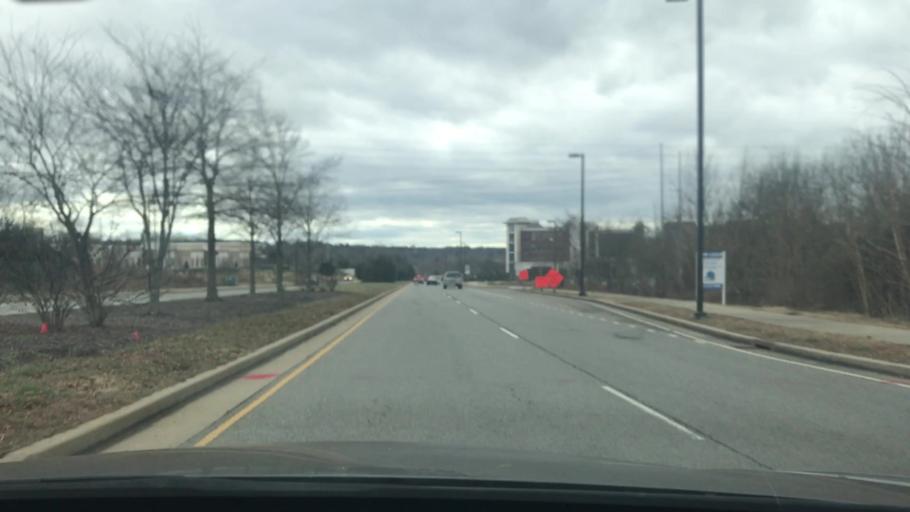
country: US
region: Tennessee
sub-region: Williamson County
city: Franklin
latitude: 35.9228
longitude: -86.8168
